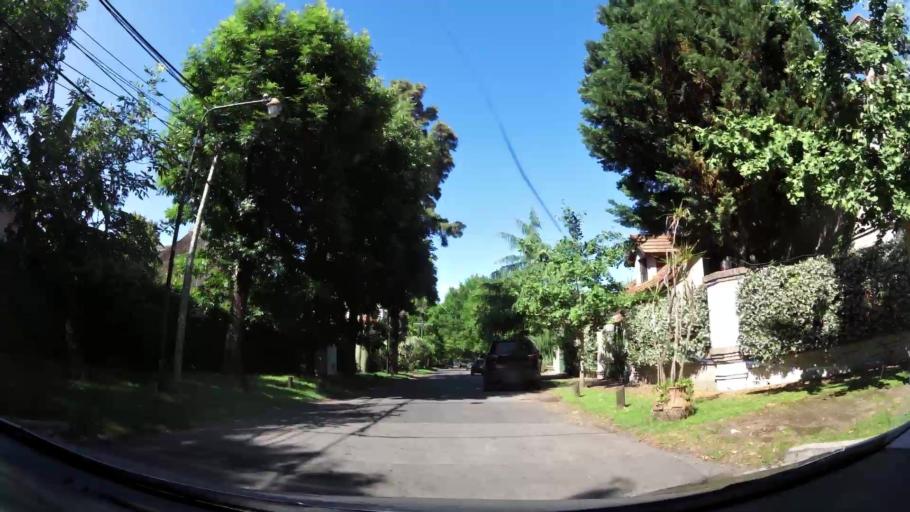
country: AR
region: Buenos Aires
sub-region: Partido de Tigre
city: Tigre
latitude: -34.4805
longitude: -58.5776
